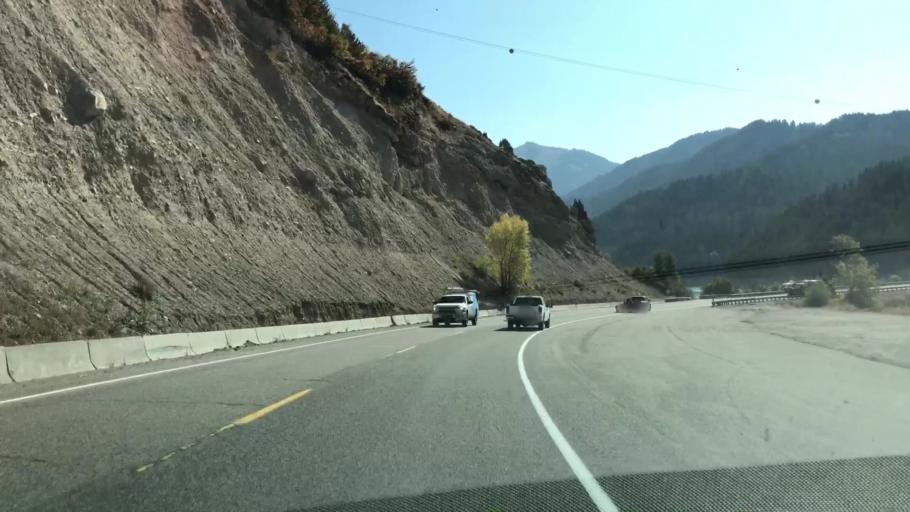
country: US
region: Idaho
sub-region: Teton County
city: Victor
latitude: 43.3202
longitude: -111.1477
